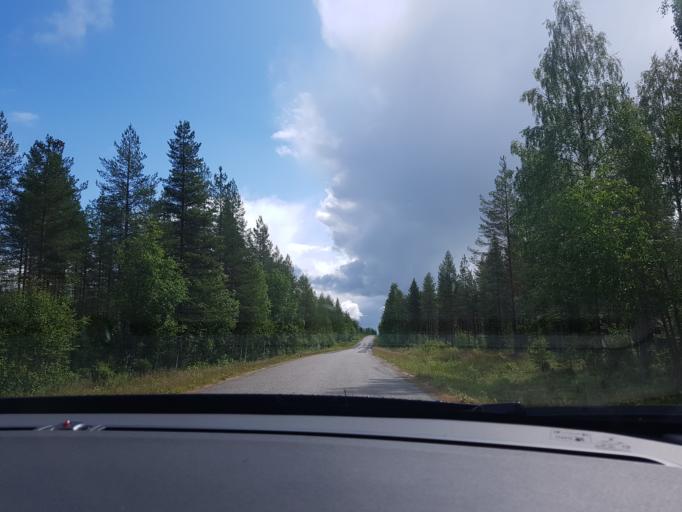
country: FI
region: Kainuu
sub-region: Kehys-Kainuu
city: Kuhmo
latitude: 64.4592
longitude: 29.6388
